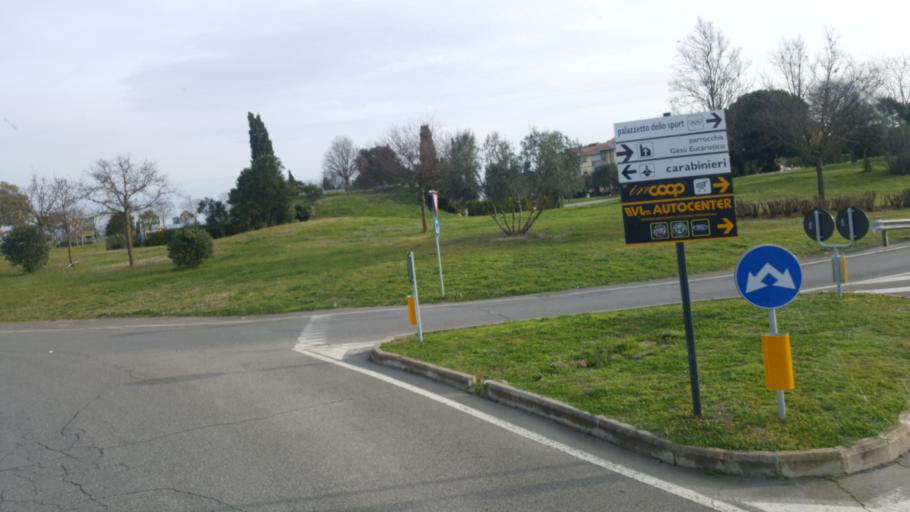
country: IT
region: Latium
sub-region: Provincia di Viterbo
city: Montalto di Castro
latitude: 42.3482
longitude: 11.6125
